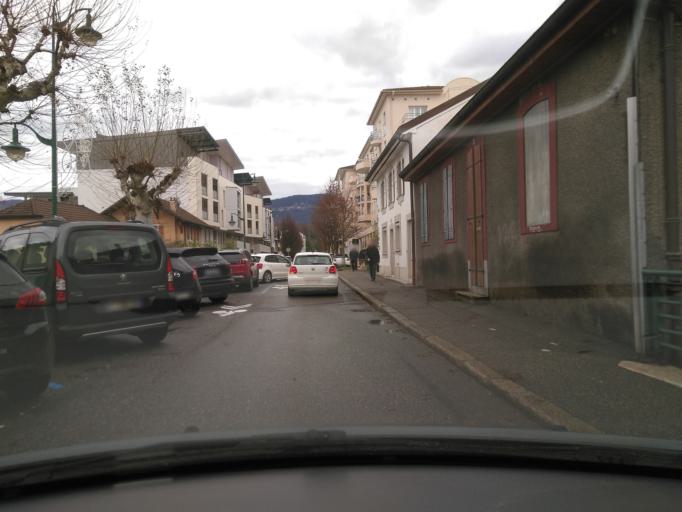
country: FR
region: Rhone-Alpes
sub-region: Departement de la Haute-Savoie
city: Saint-Julien-en-Genevois
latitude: 46.1427
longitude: 6.0807
